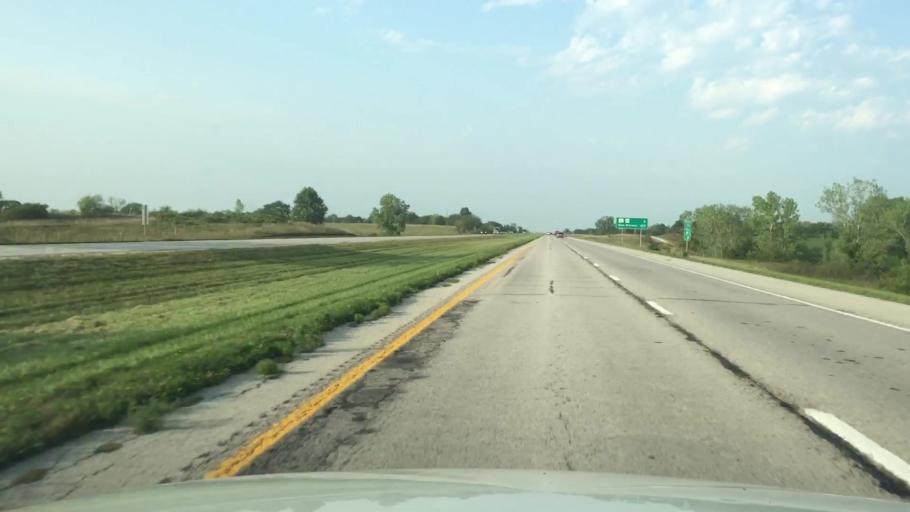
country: US
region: Missouri
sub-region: Harrison County
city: Bethany
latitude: 40.1222
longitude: -94.0572
